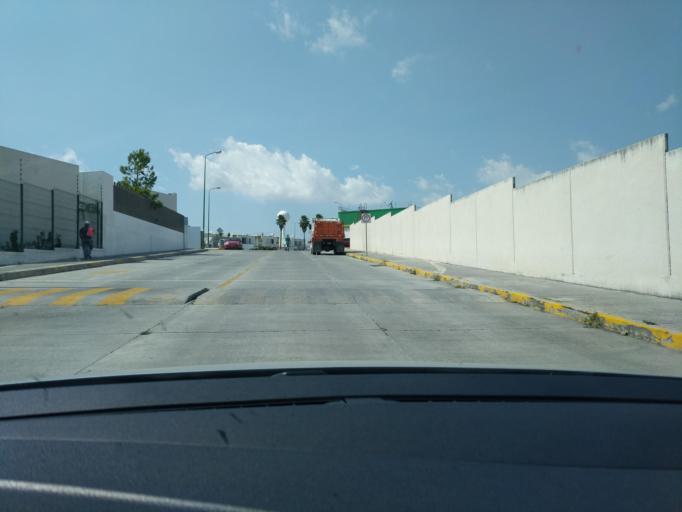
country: MX
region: Puebla
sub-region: Puebla
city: Galaxia la Calera
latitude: 19.0046
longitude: -98.1475
